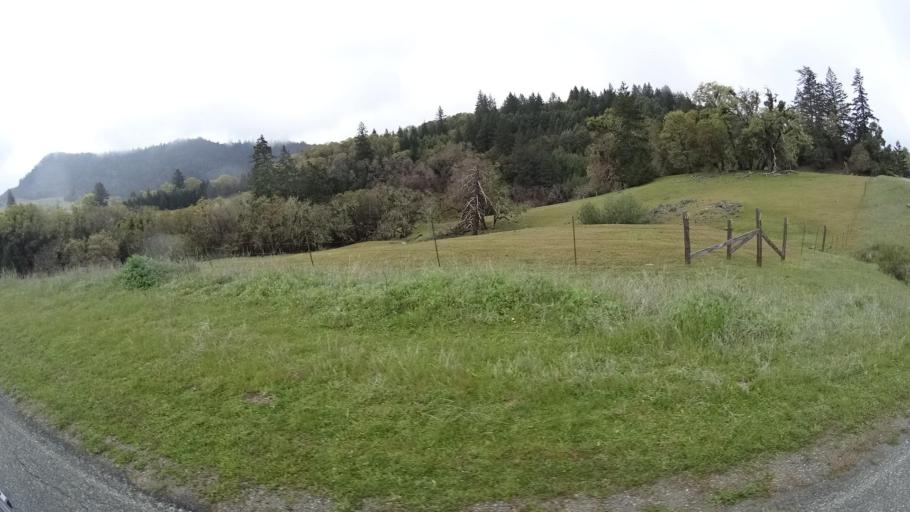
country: US
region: California
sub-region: Humboldt County
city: Redway
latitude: 40.1567
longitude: -123.5458
